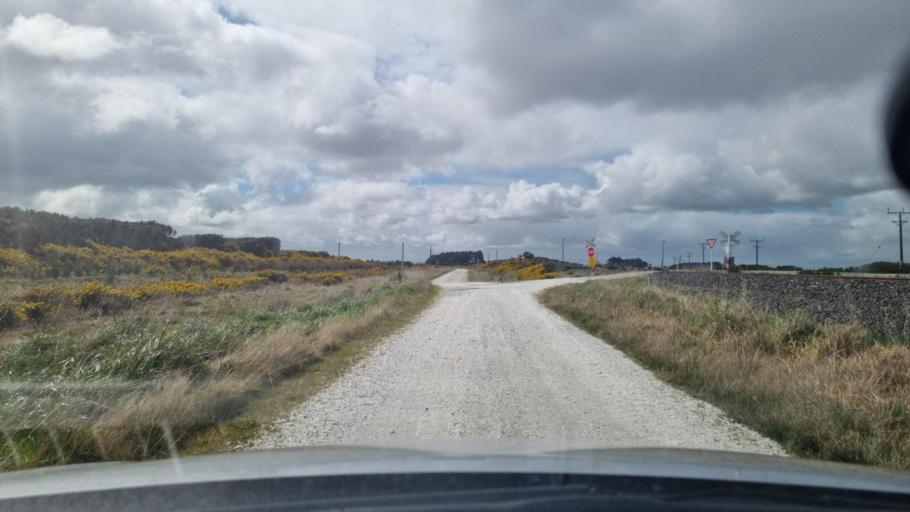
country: NZ
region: Southland
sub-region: Invercargill City
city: Bluff
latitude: -46.5280
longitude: 168.3068
